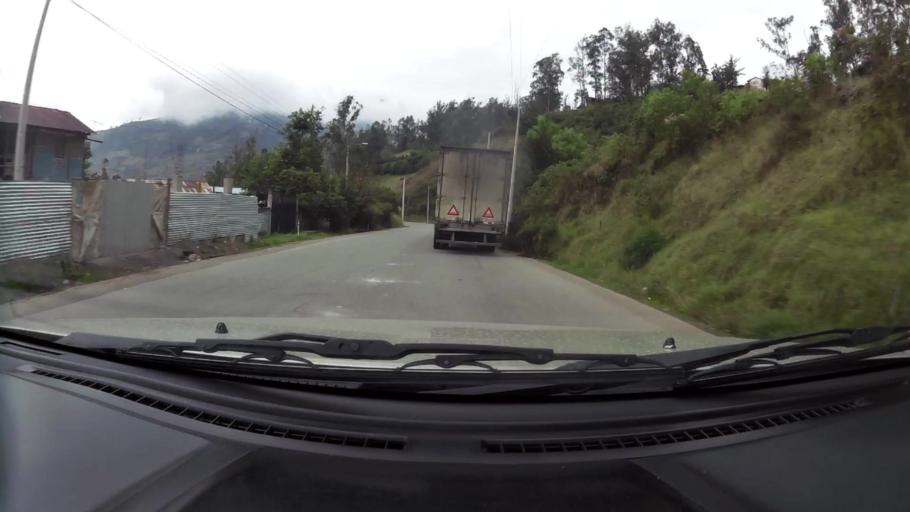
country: EC
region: Chimborazo
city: Alausi
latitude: -2.3076
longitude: -78.9212
